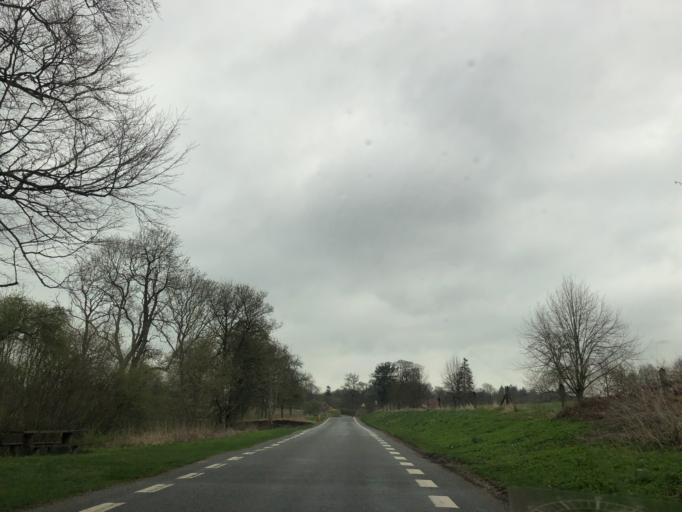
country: DK
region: Zealand
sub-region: Lejre Kommune
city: Kirke Hvalso
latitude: 55.5318
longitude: 11.8499
